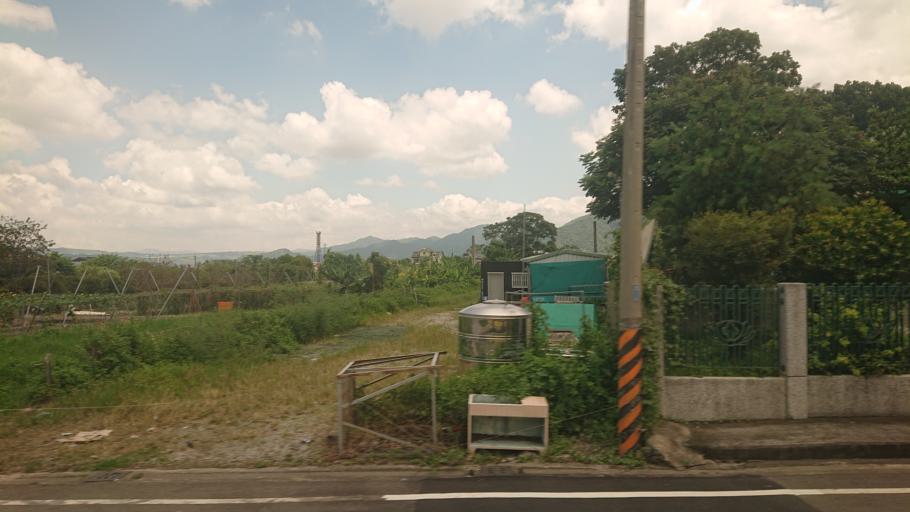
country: TW
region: Taiwan
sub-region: Nantou
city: Puli
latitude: 23.9760
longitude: 120.9840
